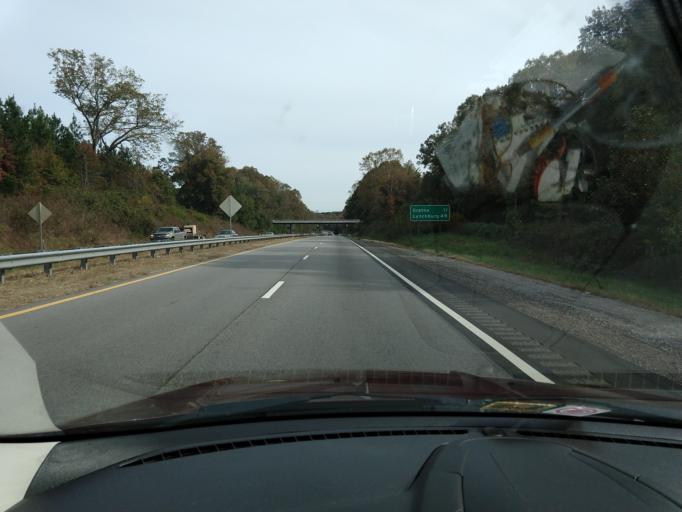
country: US
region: Virginia
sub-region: Pittsylvania County
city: Chatham
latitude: 36.8095
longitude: -79.3897
